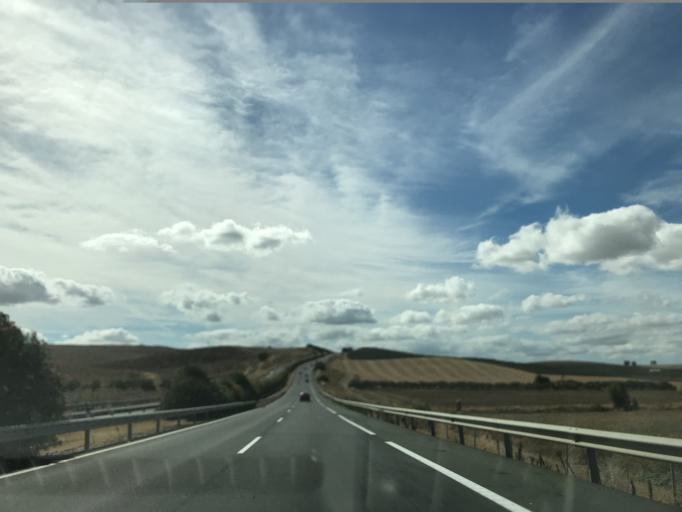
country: ES
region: Andalusia
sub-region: Province of Cordoba
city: La Victoria
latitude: 37.7340
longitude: -4.8525
